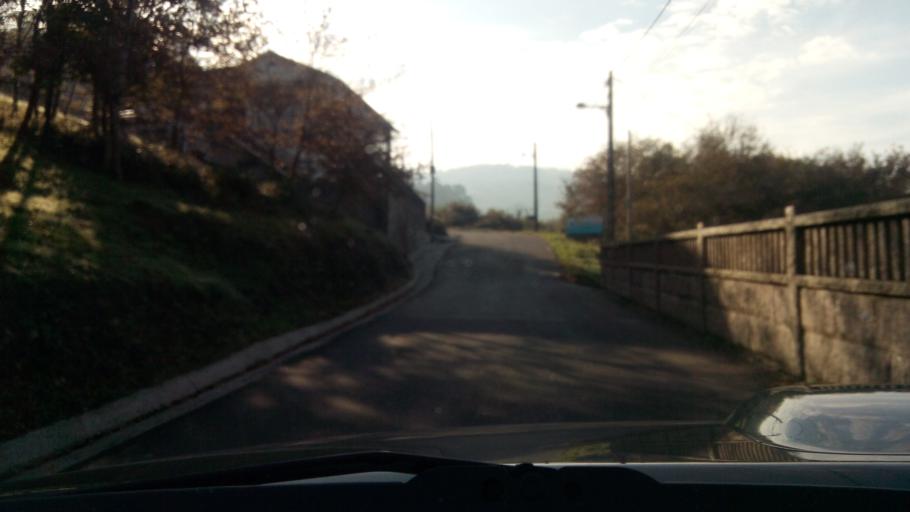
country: ES
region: Galicia
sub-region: Provincia de Pontevedra
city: Marin
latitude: 42.3615
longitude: -8.7340
